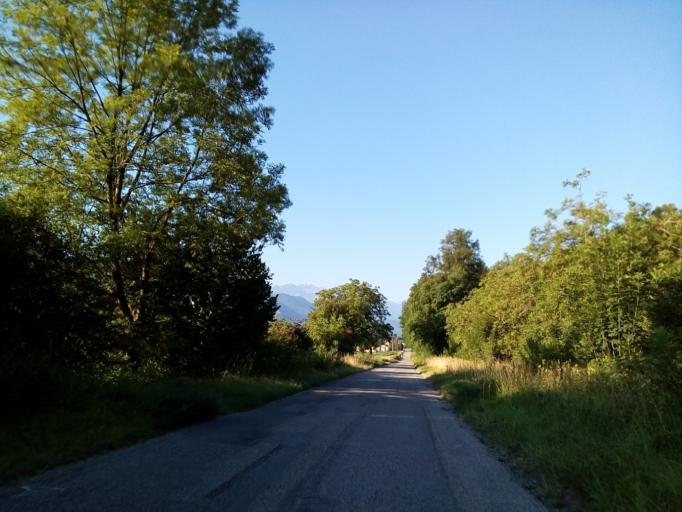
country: FR
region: Rhone-Alpes
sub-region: Departement de l'Isere
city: Barraux
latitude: 45.4189
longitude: 5.9823
